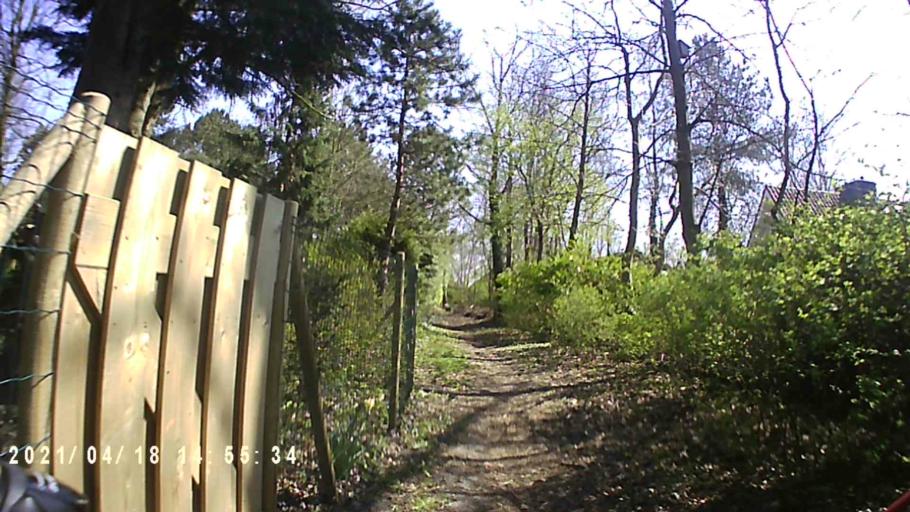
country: NL
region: Friesland
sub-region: Gemeente Dongeradeel
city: Anjum
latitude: 53.4041
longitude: 6.2197
